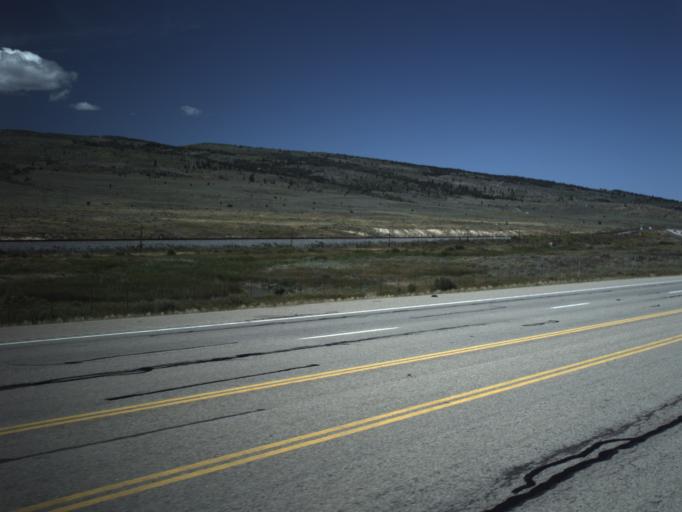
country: US
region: Utah
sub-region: Carbon County
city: Helper
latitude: 39.8737
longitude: -111.0344
